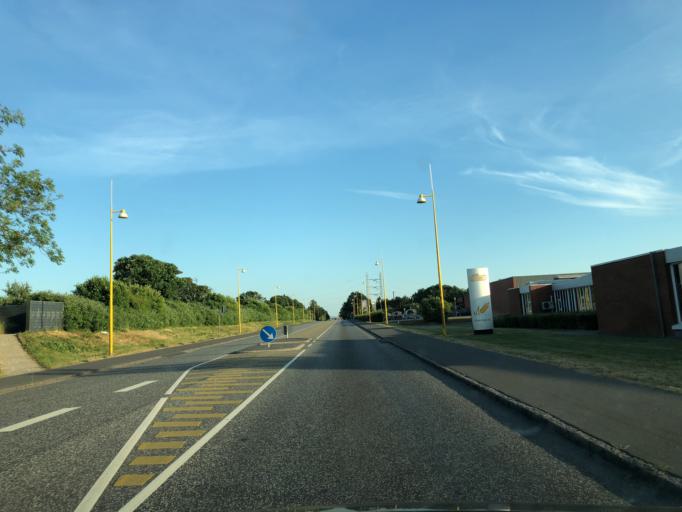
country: DK
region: Central Jutland
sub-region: Struer Kommune
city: Struer
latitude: 56.4863
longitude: 8.5836
